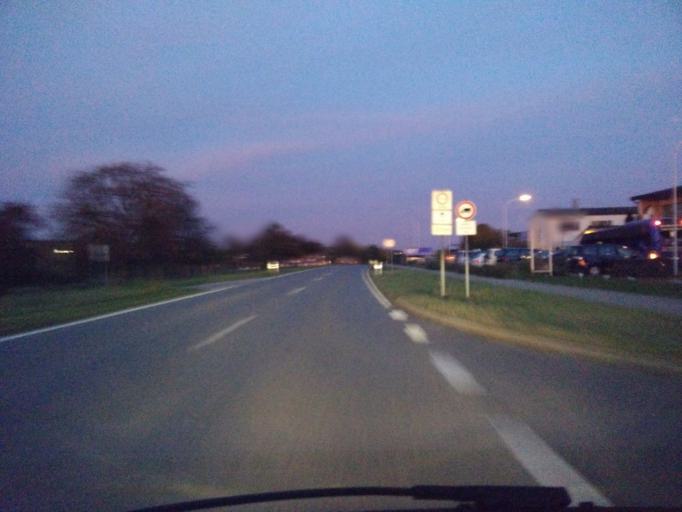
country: DE
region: Baden-Wuerttemberg
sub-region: Regierungsbezirk Stuttgart
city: Rutesheim
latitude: 48.8127
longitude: 8.9596
